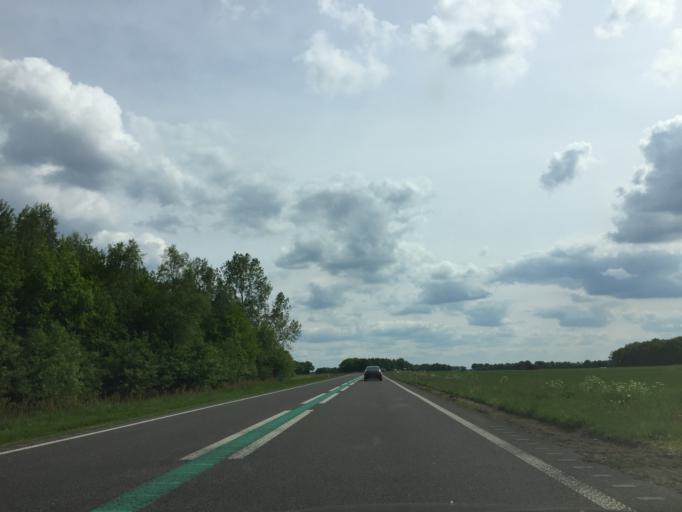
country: NL
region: Drenthe
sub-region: Gemeente Borger-Odoorn
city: Borger
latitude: 52.9515
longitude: 6.7831
